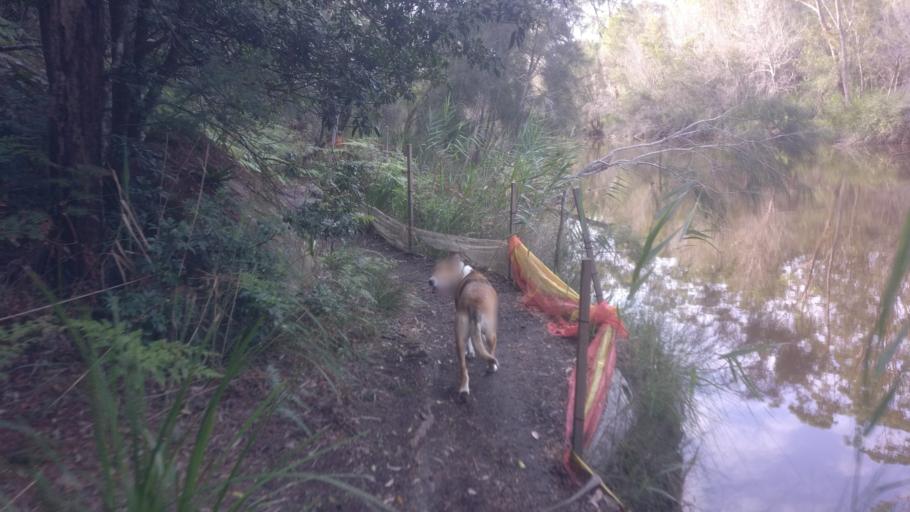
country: AU
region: New South Wales
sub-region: Pittwater
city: North Narrabeen
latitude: -33.7068
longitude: 151.2728
